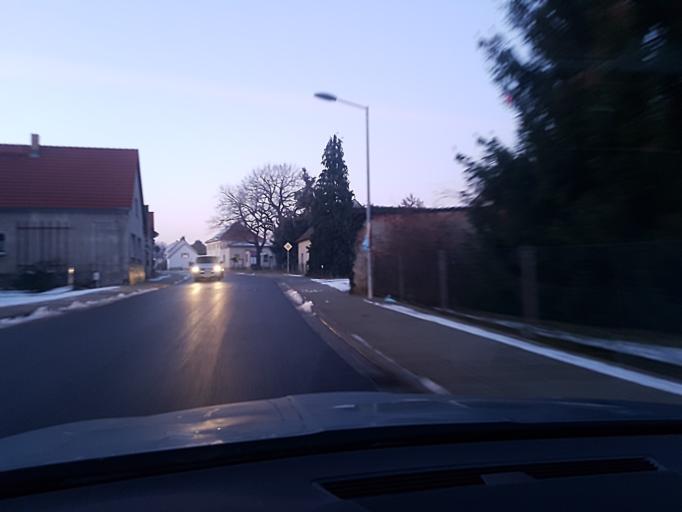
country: DE
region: Brandenburg
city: Schonborn
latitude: 51.5986
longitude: 13.4928
